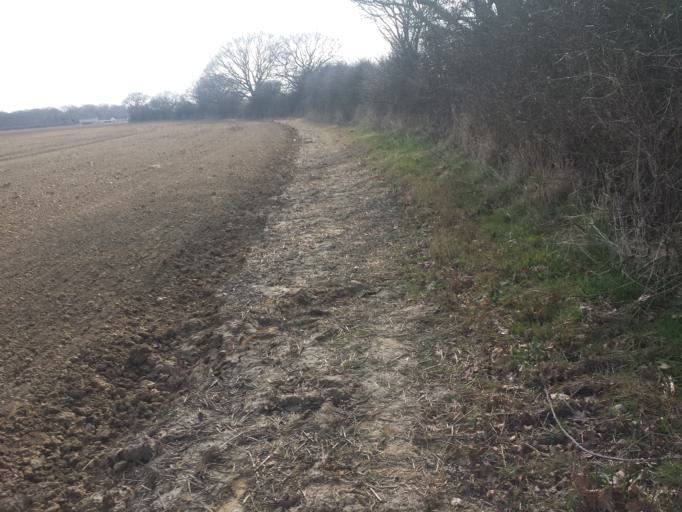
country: GB
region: England
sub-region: Essex
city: Little Clacton
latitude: 51.9015
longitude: 1.1501
